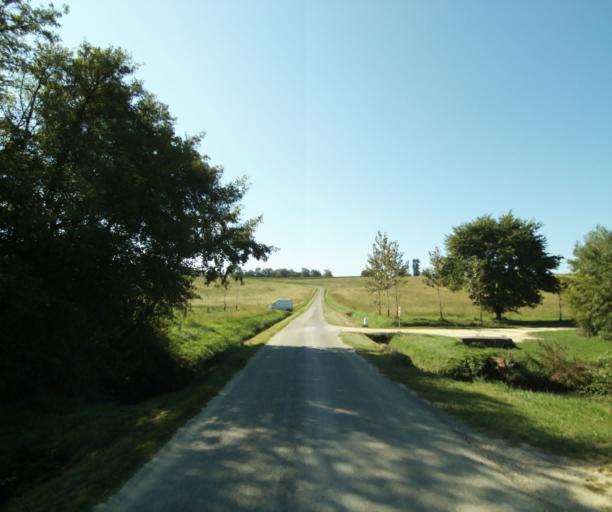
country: FR
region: Midi-Pyrenees
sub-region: Departement du Gers
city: Cazaubon
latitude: 43.9299
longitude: -0.0239
